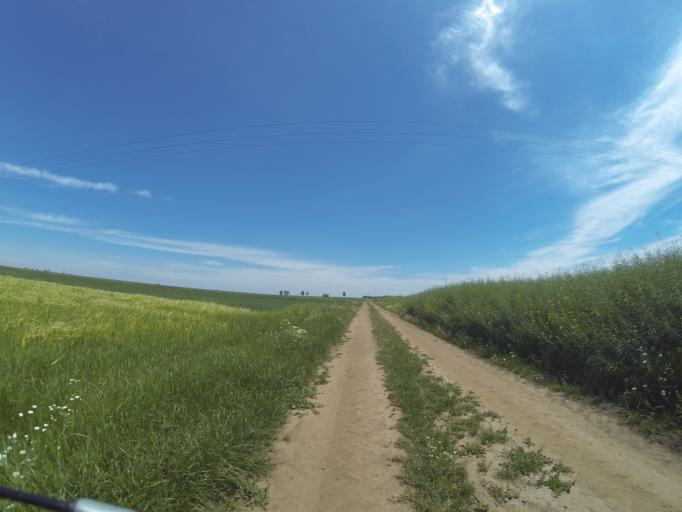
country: RO
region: Dolj
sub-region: Comuna Diosti
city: Radomir
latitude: 44.1471
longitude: 24.1528
